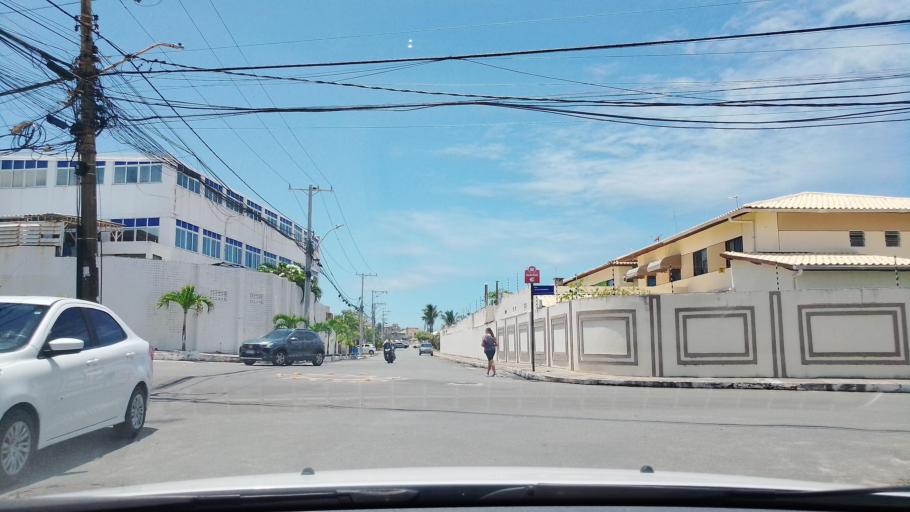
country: BR
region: Bahia
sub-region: Lauro De Freitas
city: Lauro de Freitas
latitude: -12.9372
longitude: -38.3307
